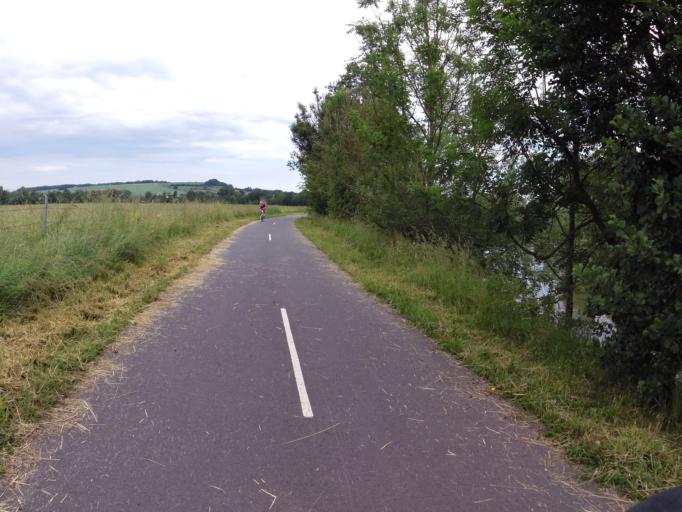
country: FR
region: Champagne-Ardenne
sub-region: Departement des Ardennes
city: Donchery
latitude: 49.6953
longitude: 4.8589
